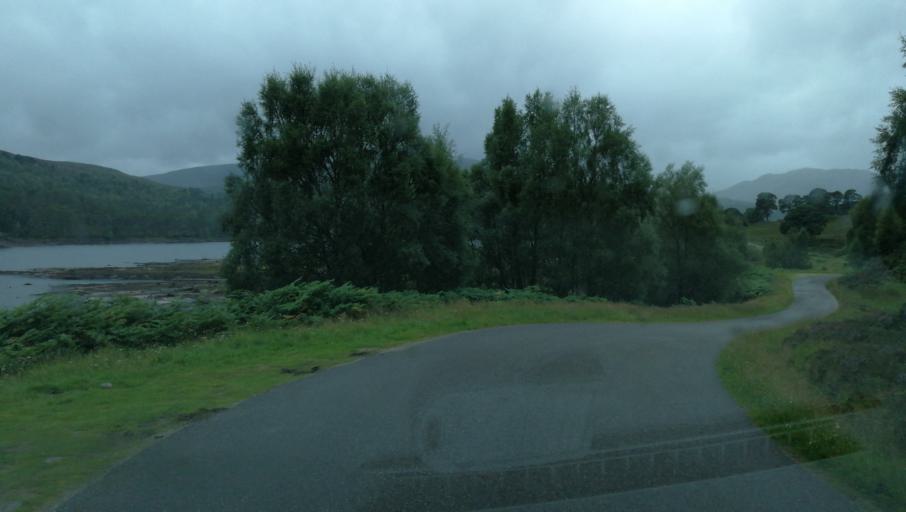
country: GB
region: Scotland
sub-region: Highland
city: Spean Bridge
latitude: 57.2716
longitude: -4.9638
